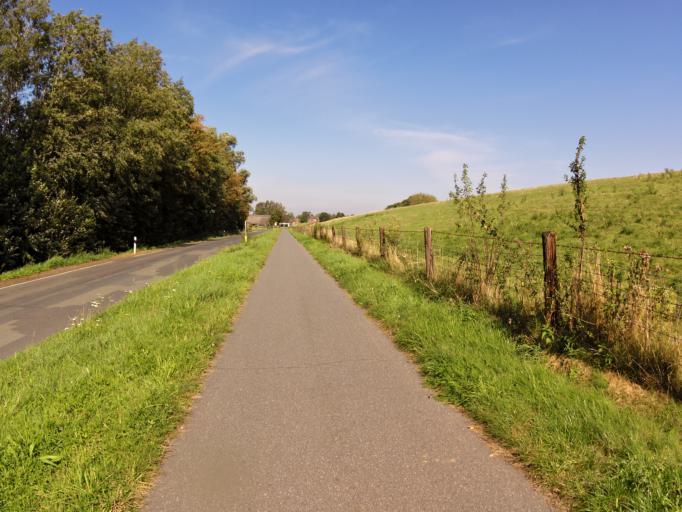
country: DE
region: Lower Saxony
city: Brake (Unterweser)
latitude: 53.2842
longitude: 8.4822
